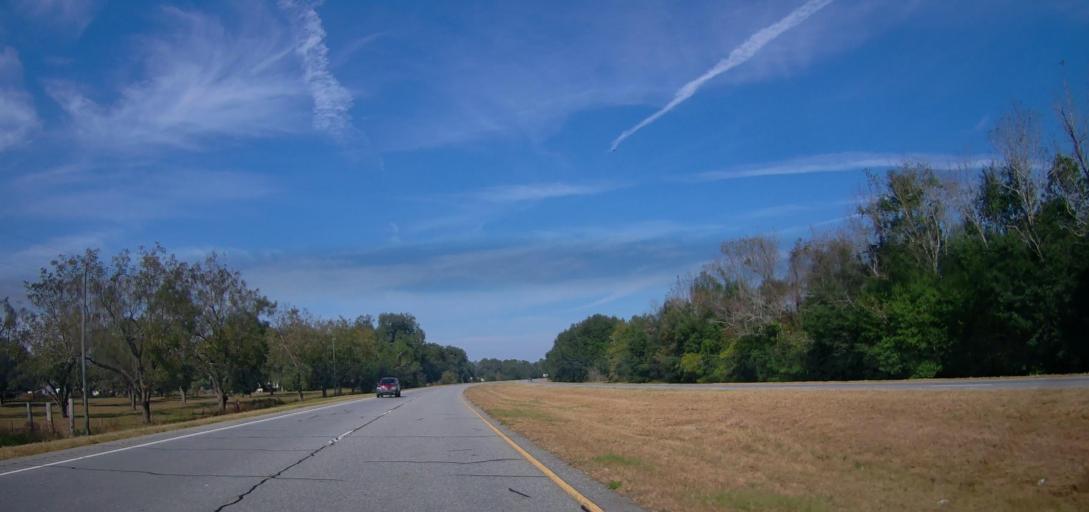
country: US
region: Georgia
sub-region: Mitchell County
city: Camilla
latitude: 31.3375
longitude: -84.1706
